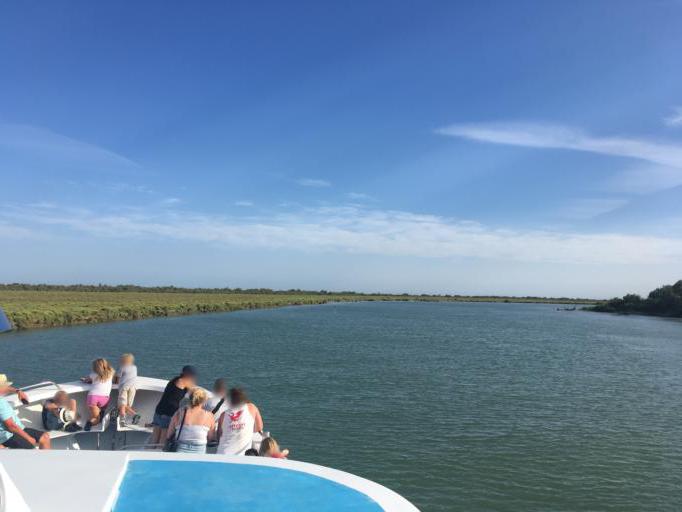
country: FR
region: Provence-Alpes-Cote d'Azur
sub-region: Departement des Bouches-du-Rhone
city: Saintes-Maries-de-la-Mer
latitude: 43.4696
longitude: 4.3895
